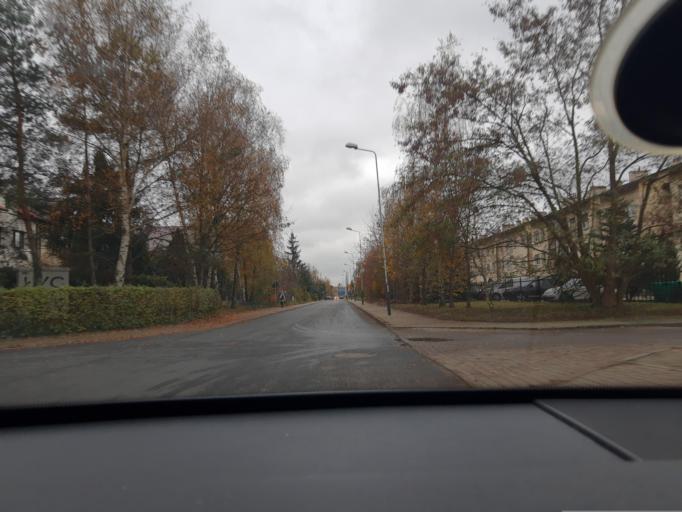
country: PL
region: Lodz Voivodeship
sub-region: Powiat pabianicki
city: Konstantynow Lodzki
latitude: 51.7392
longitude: 19.3748
